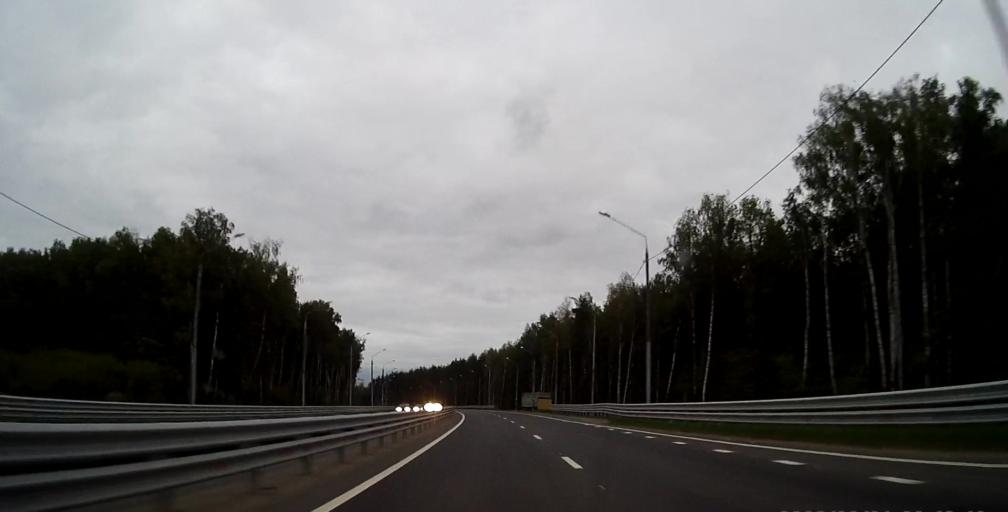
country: RU
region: Moskovskaya
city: Dubrovitsy
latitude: 55.4021
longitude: 37.5004
